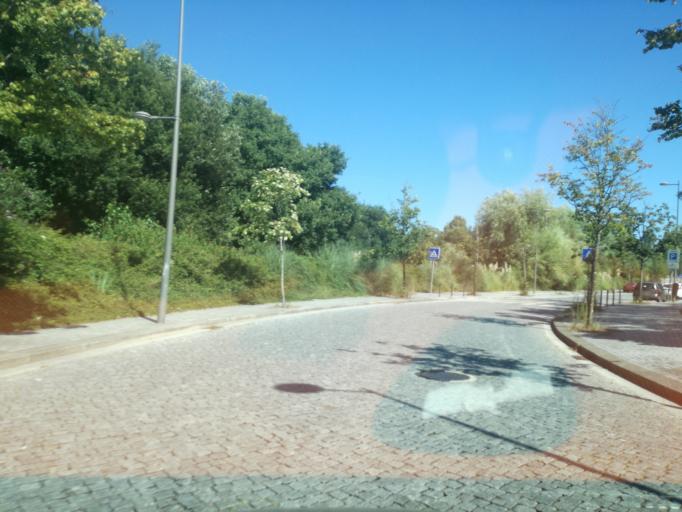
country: PT
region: Porto
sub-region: Matosinhos
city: Sao Mamede de Infesta
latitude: 41.1768
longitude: -8.6022
